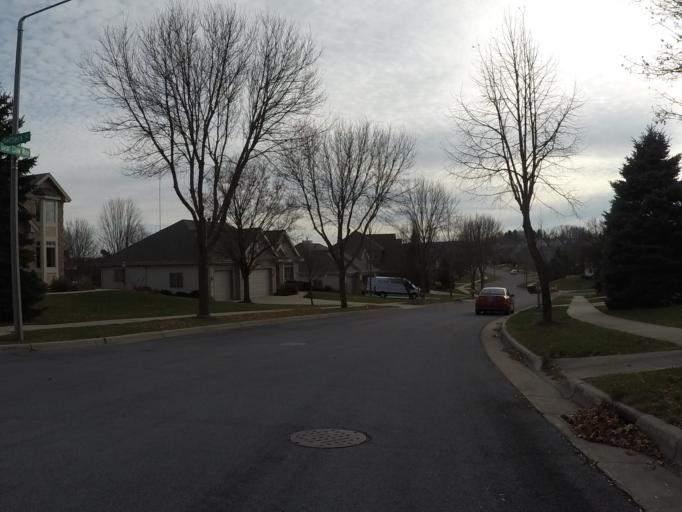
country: US
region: Wisconsin
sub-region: Dane County
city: Middleton
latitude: 43.0806
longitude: -89.5503
